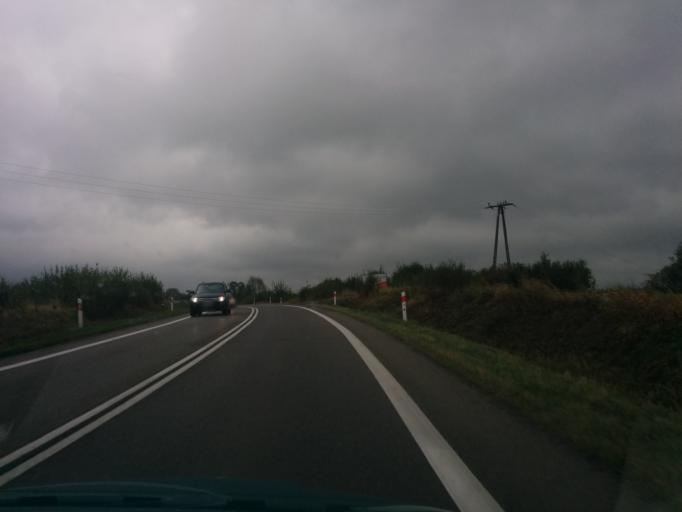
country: PL
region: Subcarpathian Voivodeship
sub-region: Powiat sanocki
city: Strachocina
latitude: 49.6022
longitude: 22.1311
